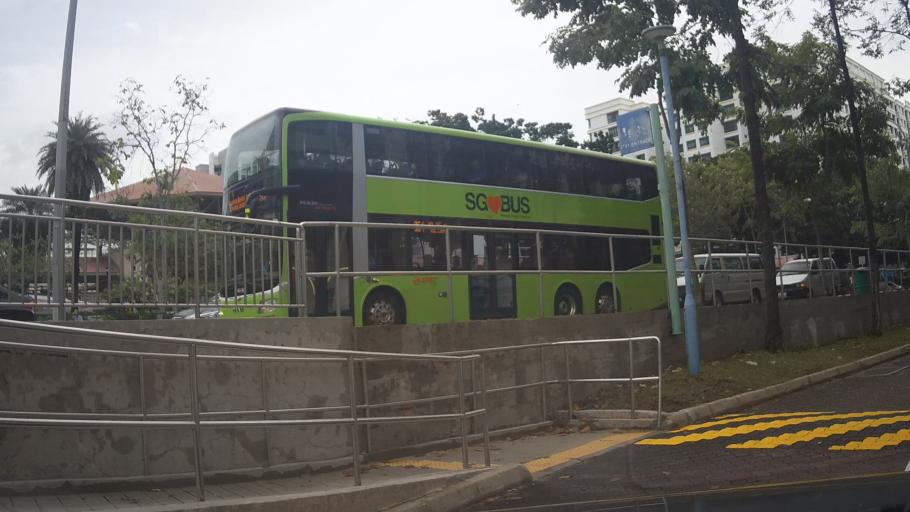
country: MY
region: Johor
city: Johor Bahru
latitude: 1.4464
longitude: 103.7990
